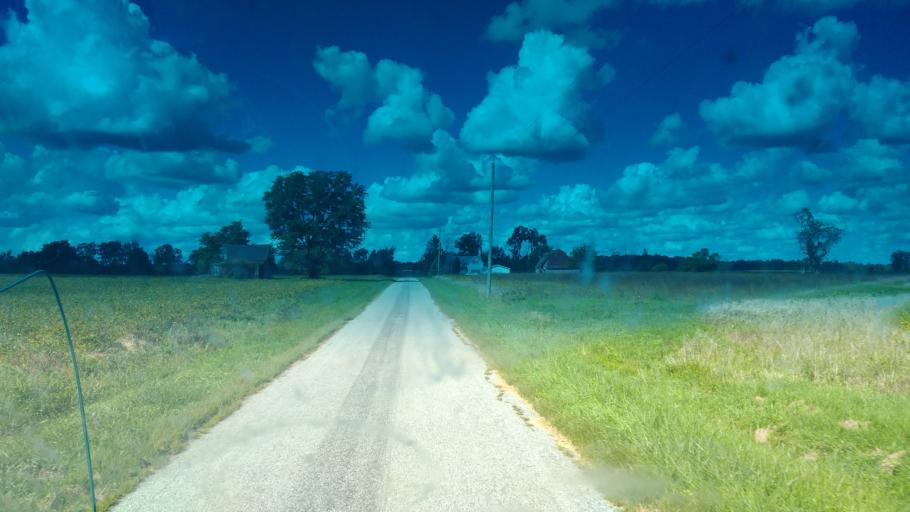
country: US
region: Ohio
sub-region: Hardin County
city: Kenton
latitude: 40.4866
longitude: -83.4995
